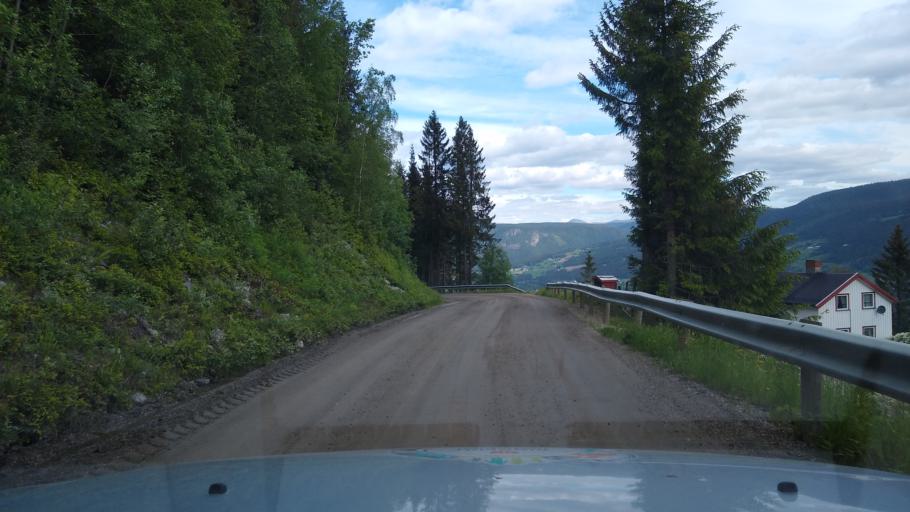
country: NO
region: Oppland
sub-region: Ringebu
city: Ringebu
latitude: 61.5002
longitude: 10.1406
